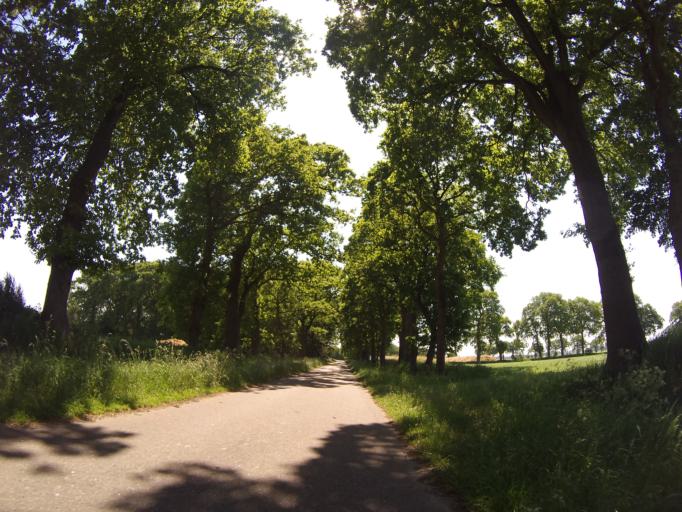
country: NL
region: Drenthe
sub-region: Gemeente Coevorden
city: Sleen
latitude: 52.7577
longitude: 6.8332
